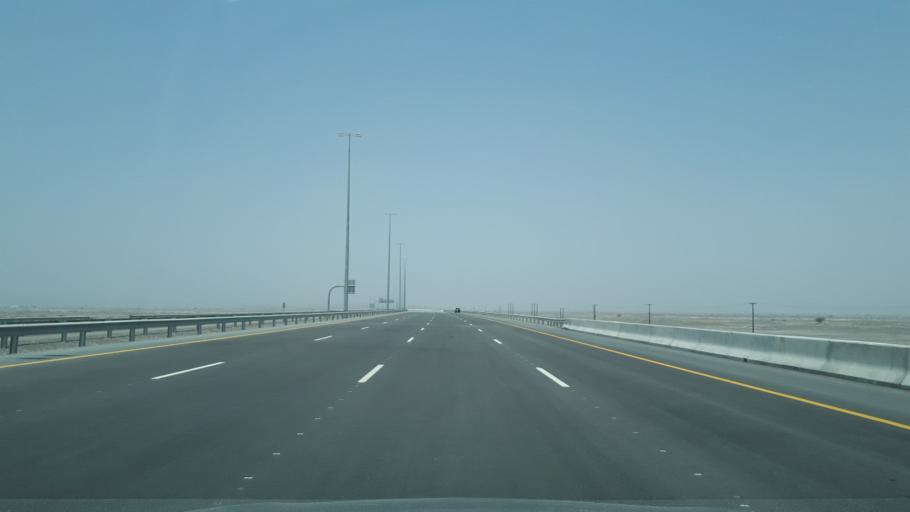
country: OM
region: Al Batinah
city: Barka'
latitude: 23.5715
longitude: 57.7159
